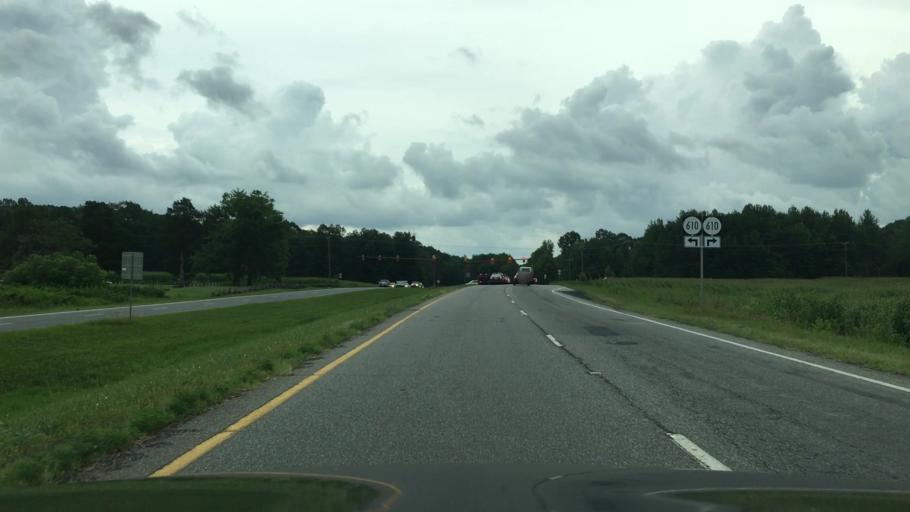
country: US
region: Virginia
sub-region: Spotsylvania County
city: Spotsylvania
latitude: 38.3086
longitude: -77.6364
